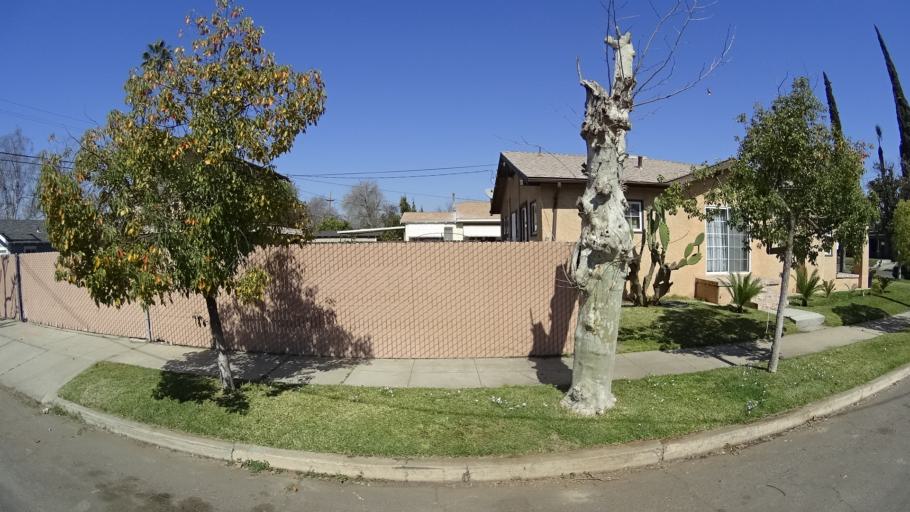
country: US
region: California
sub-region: Fresno County
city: Fresno
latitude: 36.7540
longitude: -119.8146
